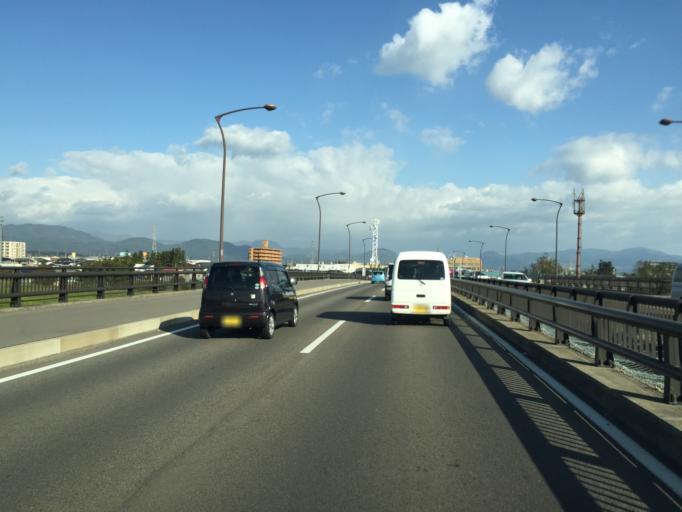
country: JP
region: Fukushima
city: Fukushima-shi
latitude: 37.7538
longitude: 140.4354
